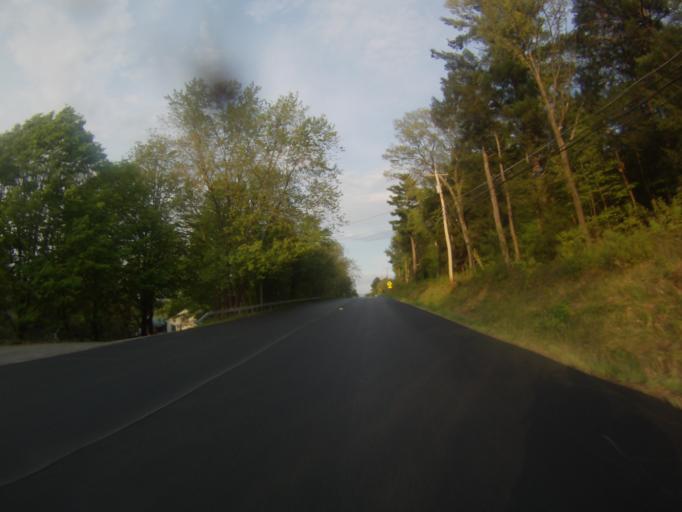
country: US
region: New York
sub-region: Essex County
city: Ticonderoga
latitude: 43.8420
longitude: -73.4554
